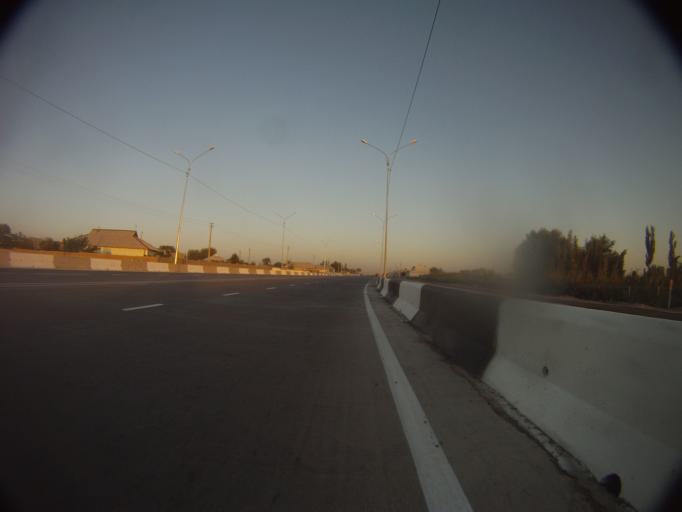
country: KZ
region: Ongtustik Qazaqstan
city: Turkestan
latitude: 43.2586
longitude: 68.3825
